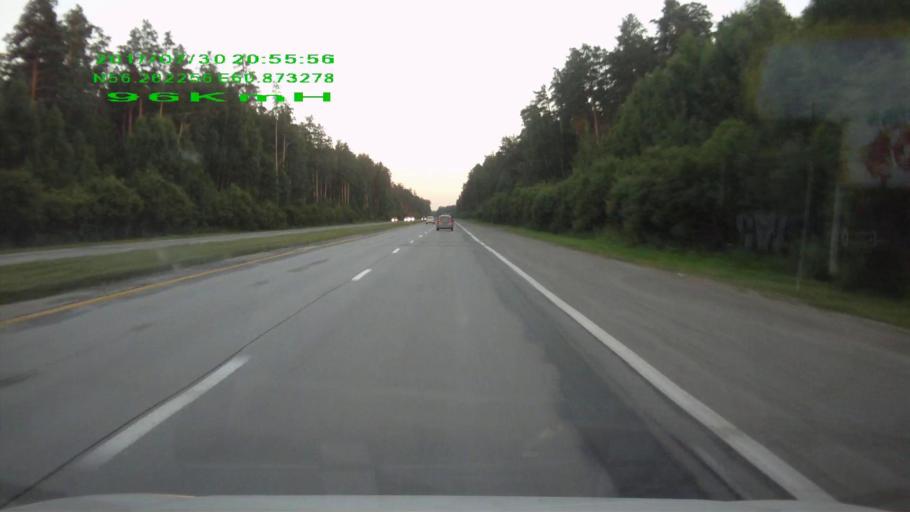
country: RU
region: Sverdlovsk
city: Shchelkun
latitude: 56.2616
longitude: 60.8732
